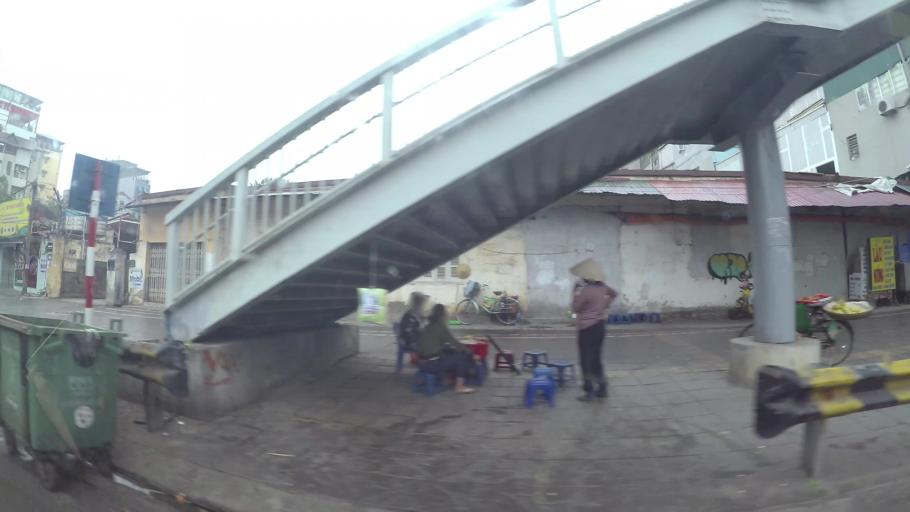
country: VN
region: Ha Noi
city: Dong Da
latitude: 21.0178
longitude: 105.8159
